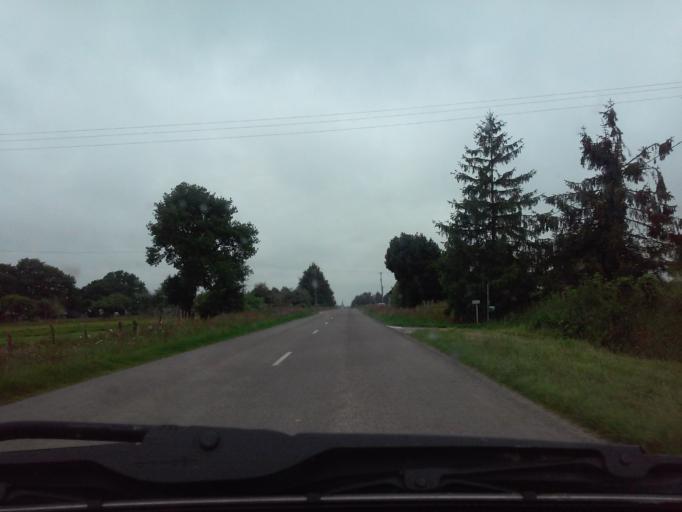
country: FR
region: Brittany
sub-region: Departement d'Ille-et-Vilaine
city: Le Pertre
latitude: 47.9634
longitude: -1.0192
